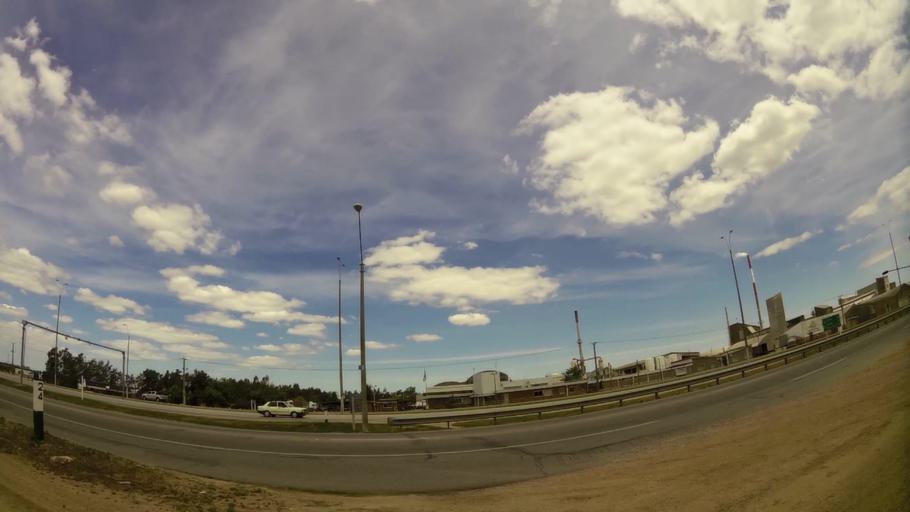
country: UY
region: San Jose
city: Delta del Tigre
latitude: -34.7757
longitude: -56.3708
